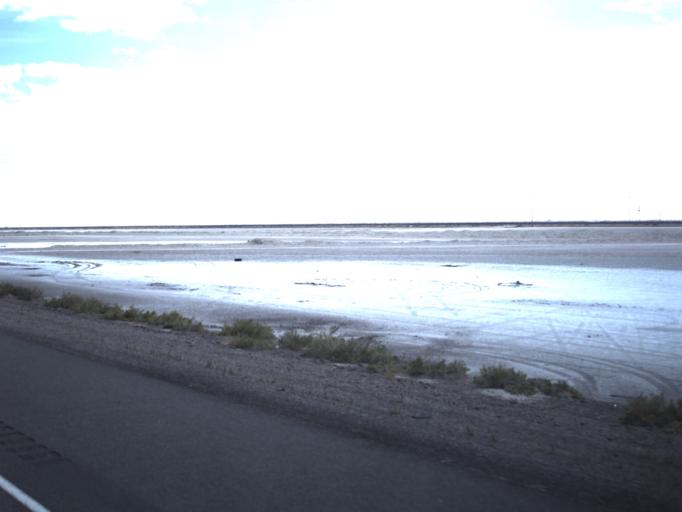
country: US
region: Utah
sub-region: Tooele County
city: Wendover
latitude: 40.7402
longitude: -113.9404
